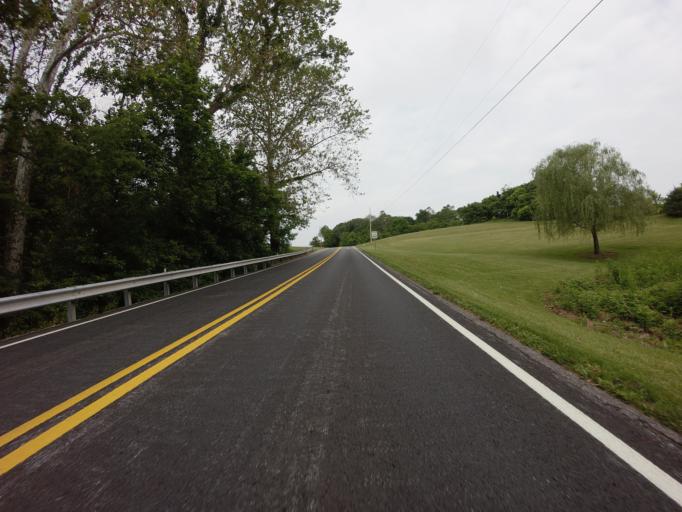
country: US
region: Maryland
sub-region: Frederick County
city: Brunswick
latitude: 39.3229
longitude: -77.5970
